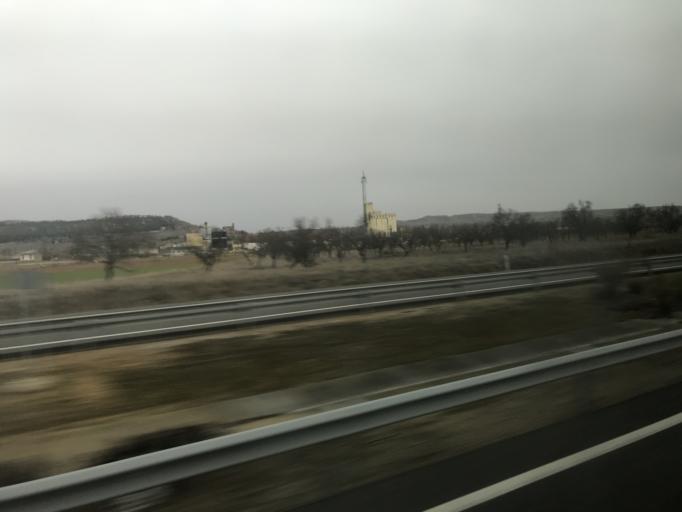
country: ES
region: Castille and Leon
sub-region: Provincia de Burgos
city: Villaquiran de los Infantes
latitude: 42.2209
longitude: -4.0043
